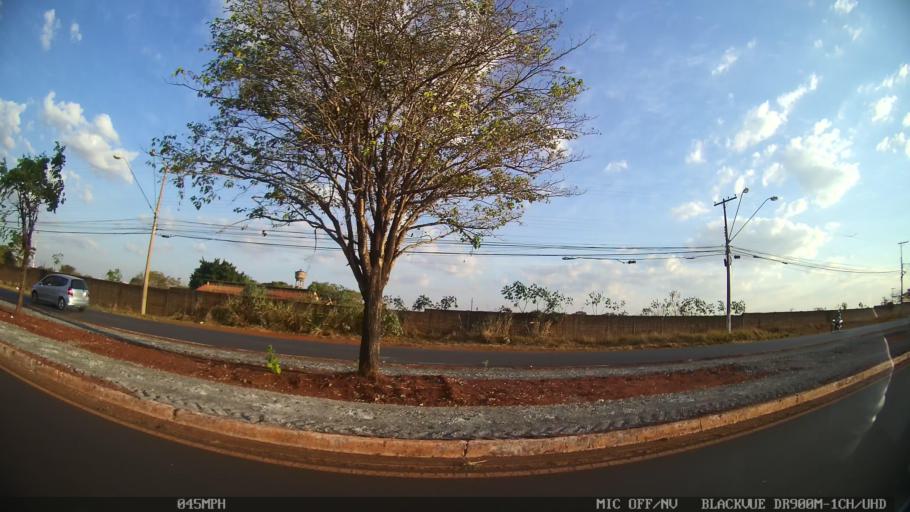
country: BR
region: Sao Paulo
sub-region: Ribeirao Preto
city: Ribeirao Preto
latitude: -21.1482
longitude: -47.7622
